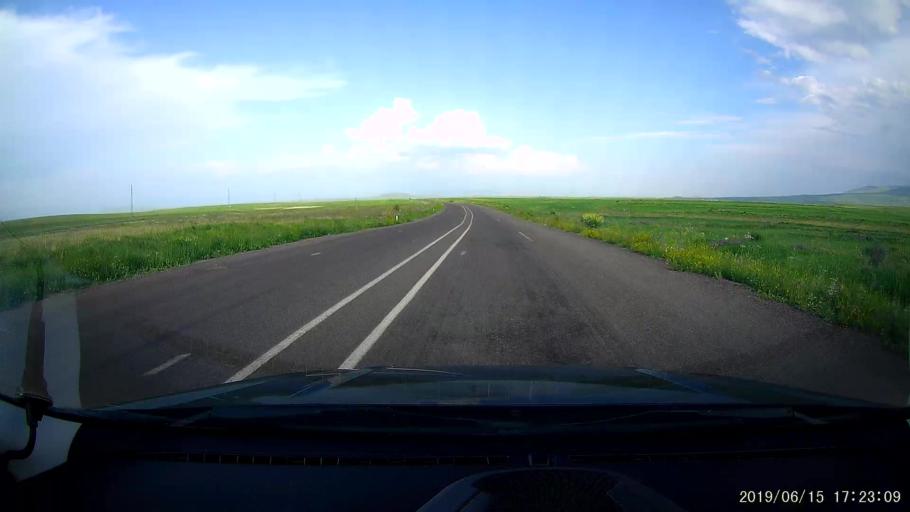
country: TR
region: Kars
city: Basgedikler
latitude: 40.6176
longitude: 43.3563
